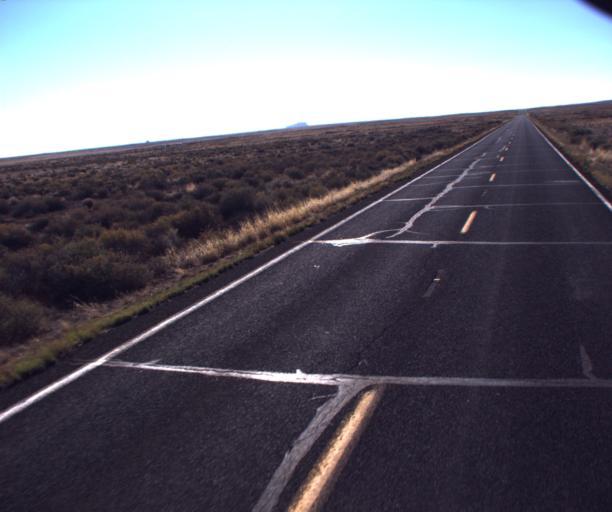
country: US
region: Arizona
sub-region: Navajo County
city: First Mesa
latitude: 35.6772
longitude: -110.4991
